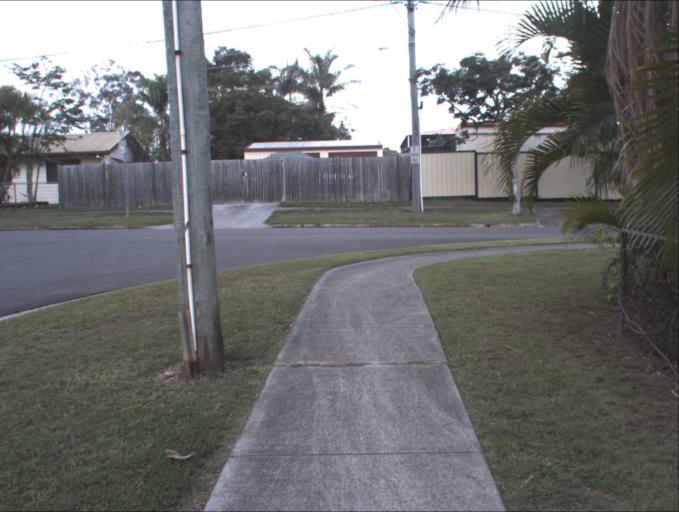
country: AU
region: Queensland
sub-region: Logan
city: Waterford West
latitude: -27.6849
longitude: 153.1318
